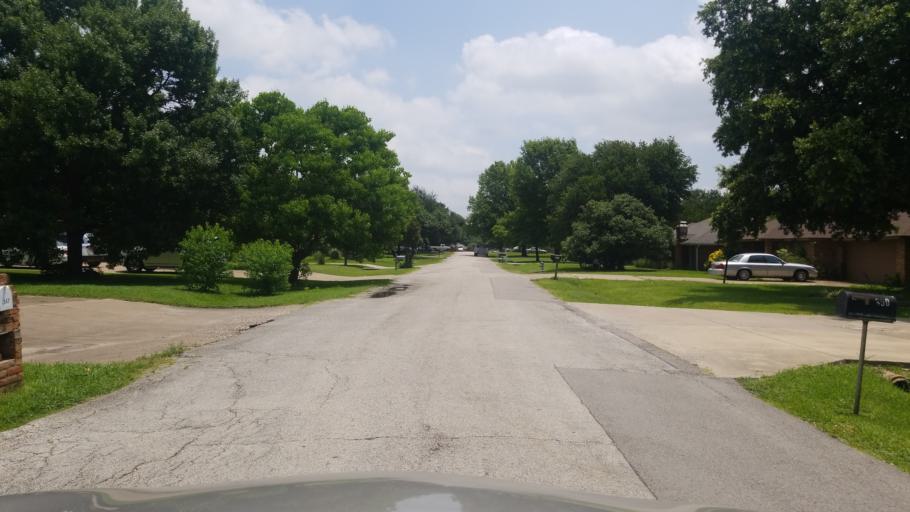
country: US
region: Texas
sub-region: Dallas County
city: Duncanville
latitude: 32.6737
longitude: -96.9130
